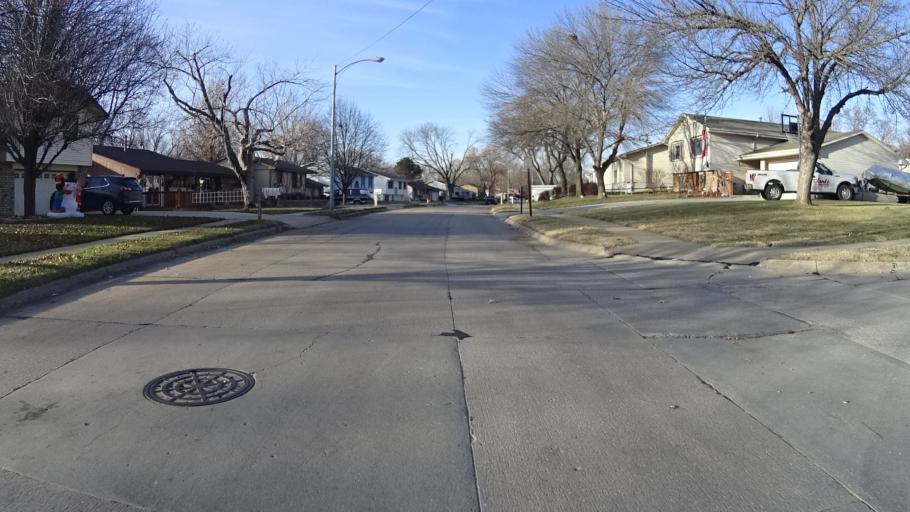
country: US
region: Nebraska
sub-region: Sarpy County
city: La Vista
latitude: 41.1867
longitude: -95.9982
